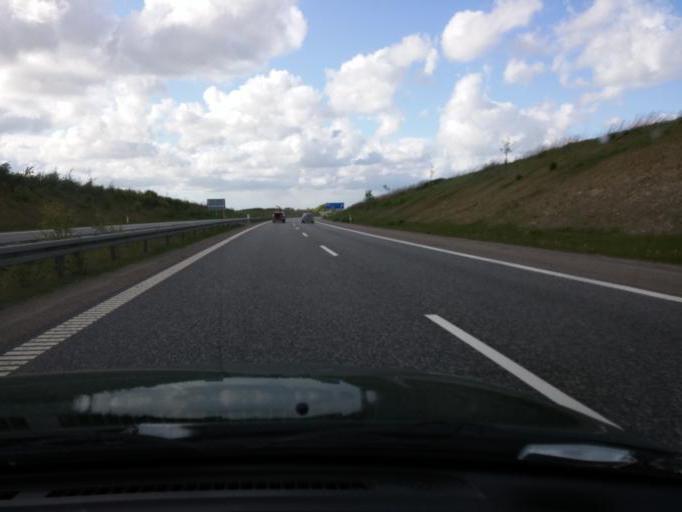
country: DK
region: South Denmark
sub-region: Faaborg-Midtfyn Kommune
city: Ringe
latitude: 55.2497
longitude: 10.4762
